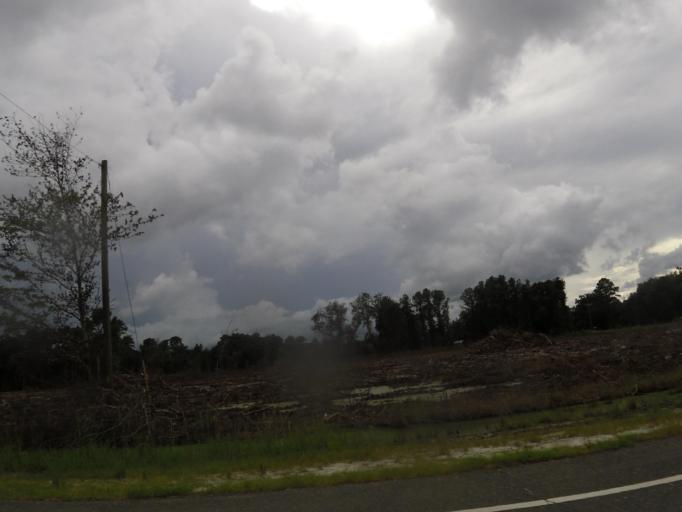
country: US
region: Florida
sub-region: Baker County
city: Macclenny
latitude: 30.5182
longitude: -82.2246
